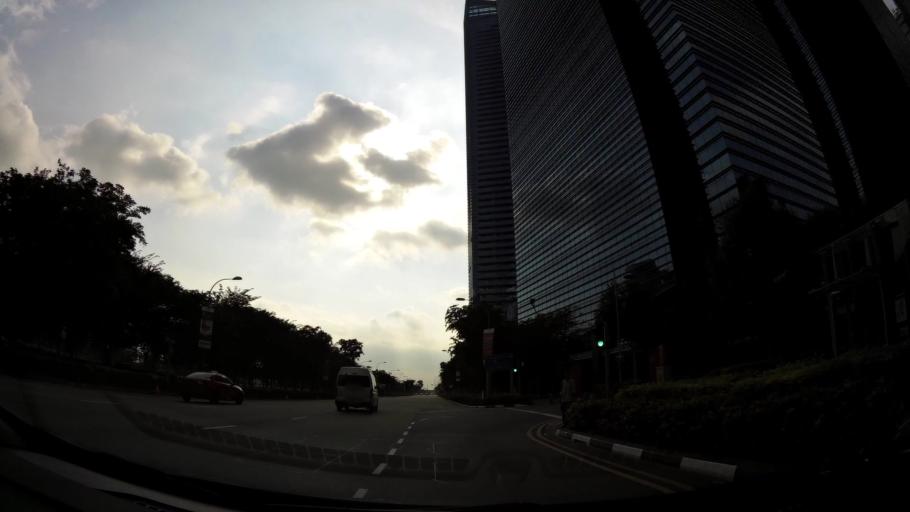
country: SG
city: Singapore
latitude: 1.2808
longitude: 103.8540
